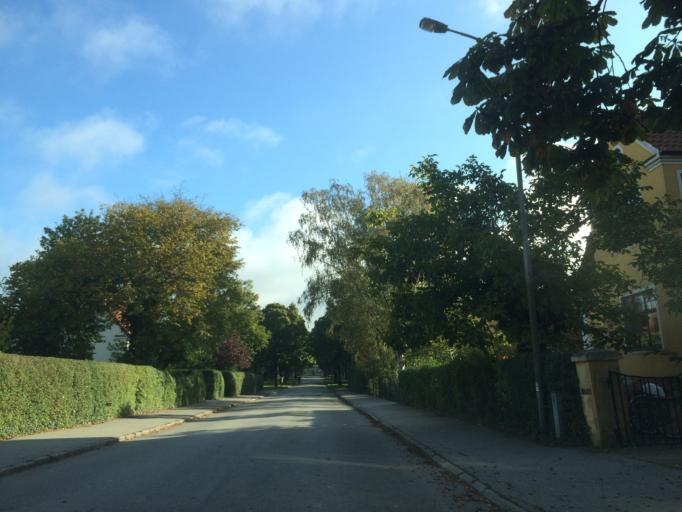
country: SE
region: Skane
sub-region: Lunds Kommun
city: Lund
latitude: 55.7040
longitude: 13.2074
